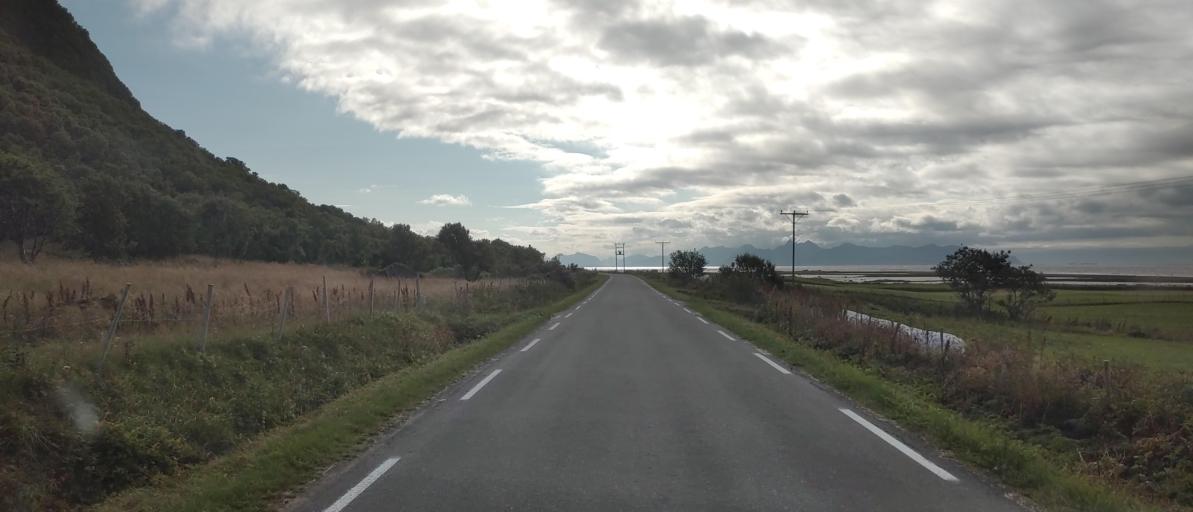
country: NO
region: Nordland
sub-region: Sortland
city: Sortland
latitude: 69.0708
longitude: 15.5477
